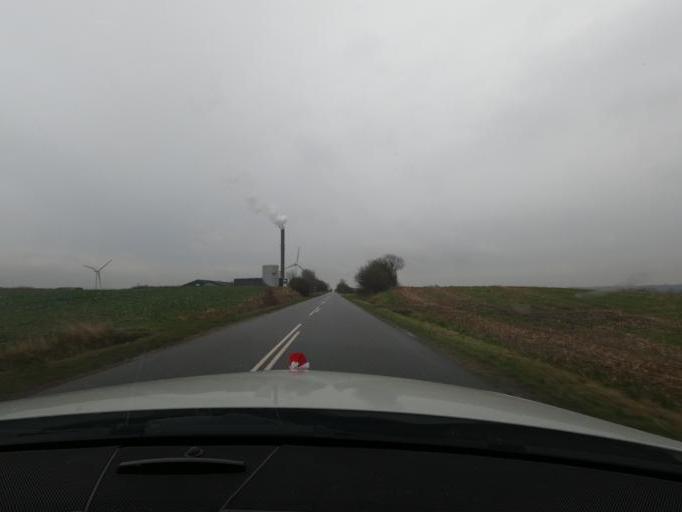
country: DK
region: South Denmark
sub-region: Haderslev Kommune
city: Haderslev
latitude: 55.2016
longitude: 9.4529
